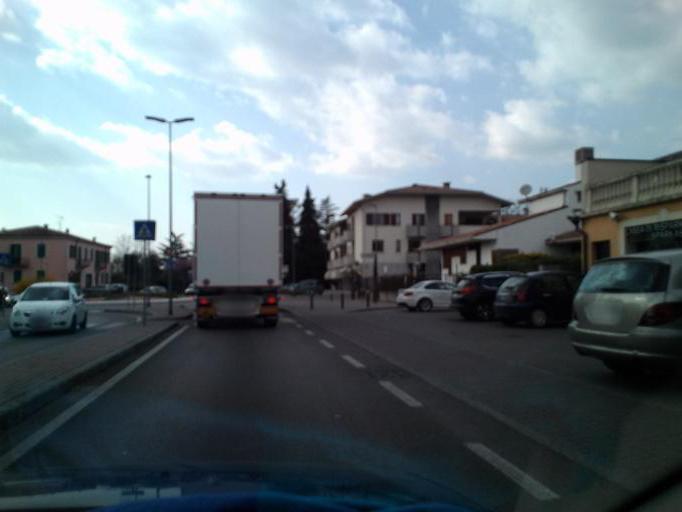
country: IT
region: Veneto
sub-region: Provincia di Verona
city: San Pietro in Cariano
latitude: 45.5211
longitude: 10.8861
